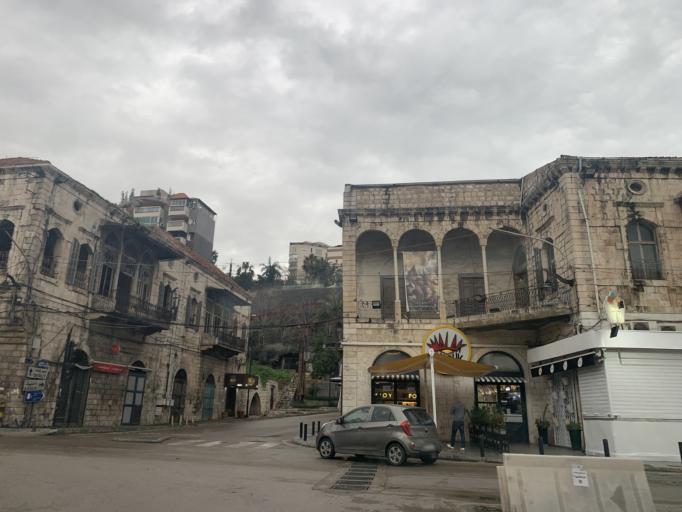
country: LB
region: Mont-Liban
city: Djounie
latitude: 33.9823
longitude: 35.6266
